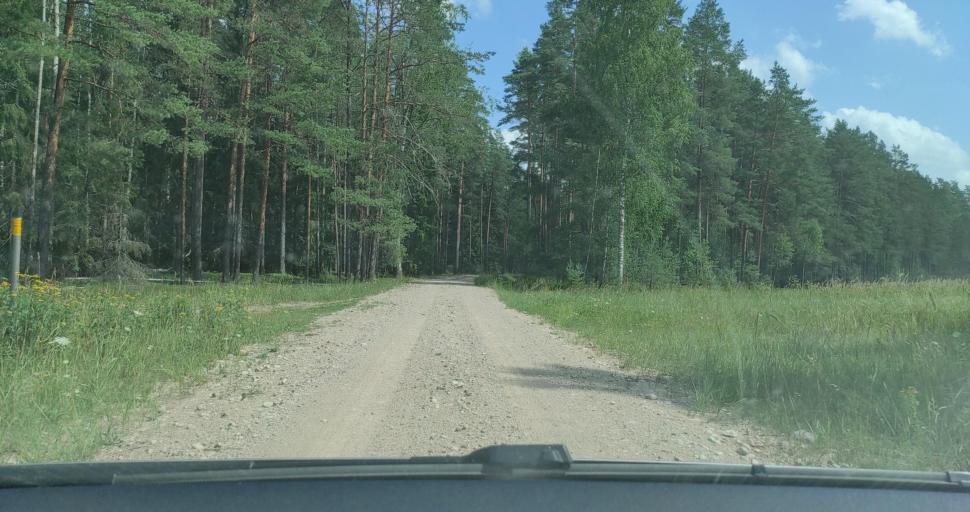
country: LV
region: Kuldigas Rajons
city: Kuldiga
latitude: 57.0677
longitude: 22.2202
